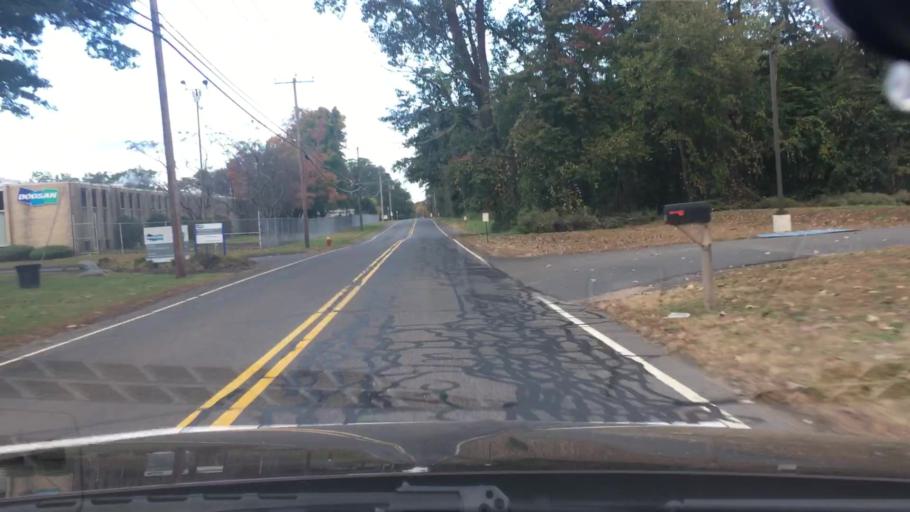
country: US
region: Connecticut
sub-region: Hartford County
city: South Windsor
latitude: 41.8335
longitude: -72.6067
